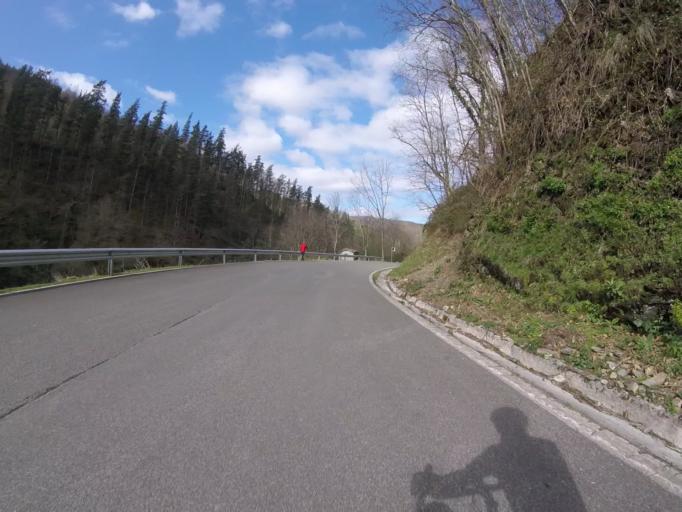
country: ES
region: Navarre
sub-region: Provincia de Navarra
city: Goizueta
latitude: 43.1643
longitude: -1.8543
